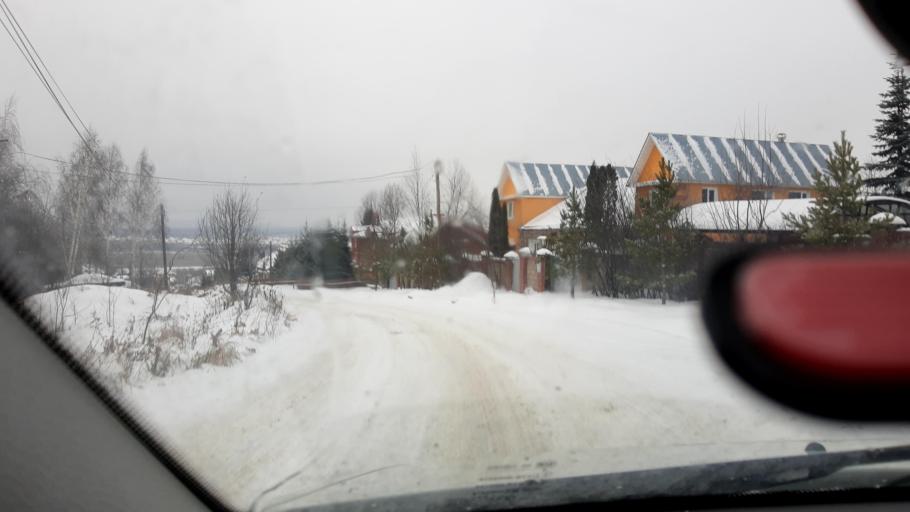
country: RU
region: Bashkortostan
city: Kabakovo
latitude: 54.6334
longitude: 56.0838
